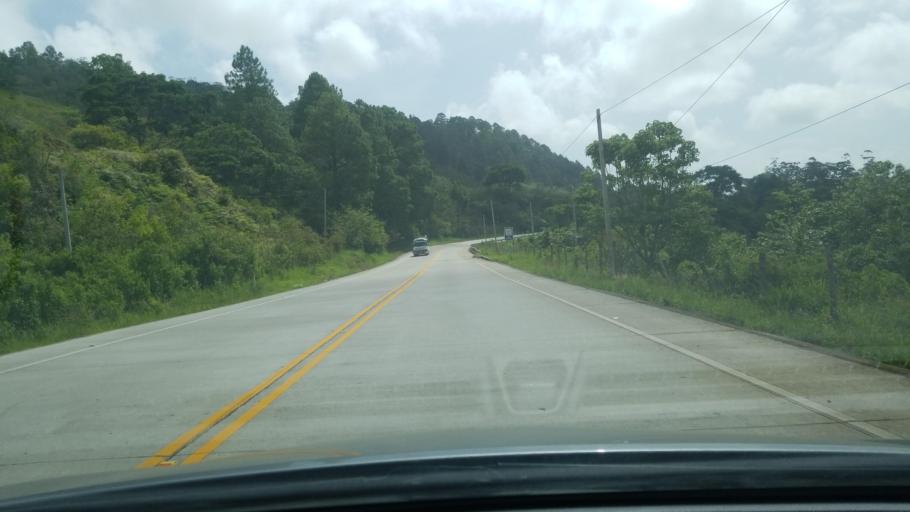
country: HN
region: Copan
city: San Jeronimo
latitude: 14.9327
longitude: -88.9341
